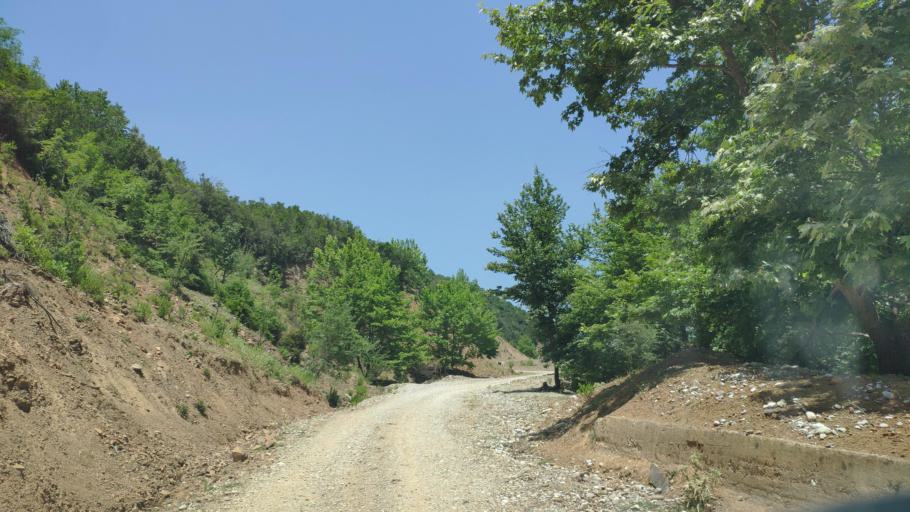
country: GR
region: Thessaly
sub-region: Nomos Kardhitsas
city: Anthiro
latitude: 39.1694
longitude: 21.3718
